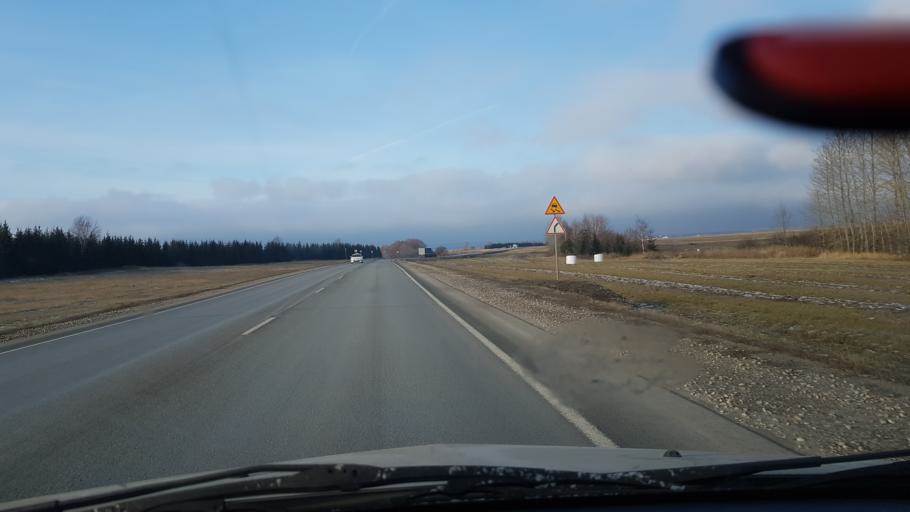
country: RU
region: Tatarstan
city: Laishevo
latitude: 55.3973
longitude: 49.7721
